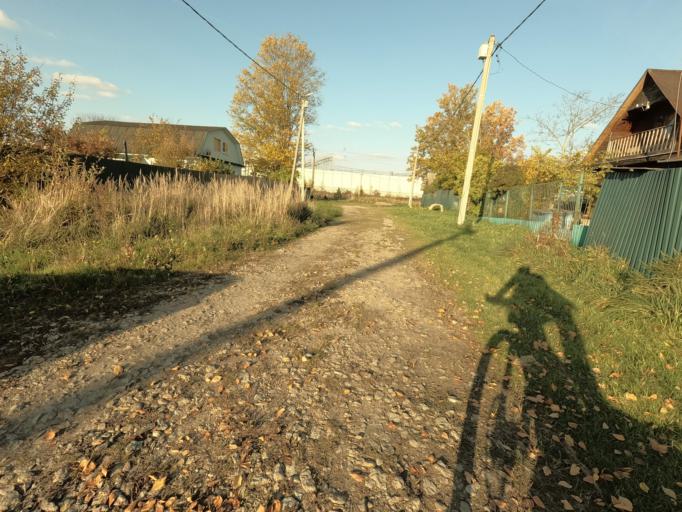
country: RU
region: Leningrad
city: Mga
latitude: 59.7553
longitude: 31.0522
